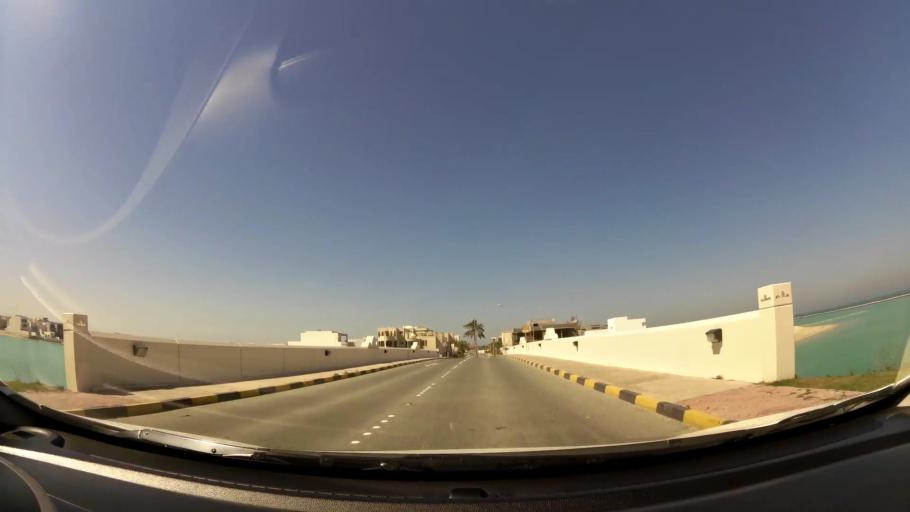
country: BH
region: Muharraq
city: Al Hadd
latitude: 26.2928
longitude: 50.6737
